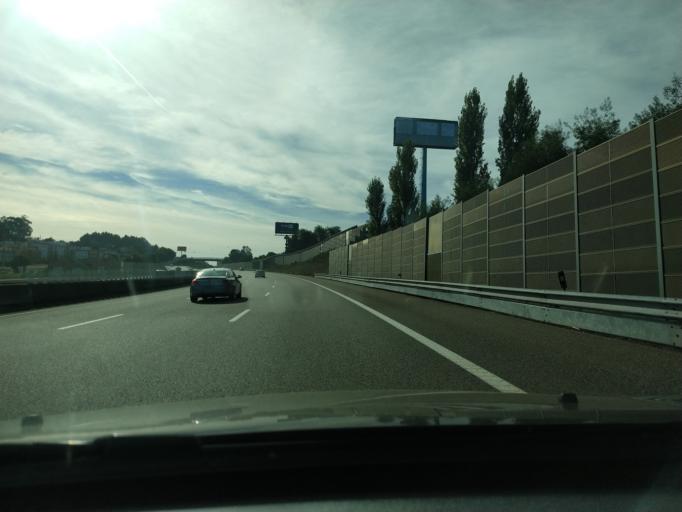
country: PT
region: Aveiro
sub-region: Santa Maria da Feira
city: Pacos de Brandao
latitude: 40.9764
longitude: -8.5758
